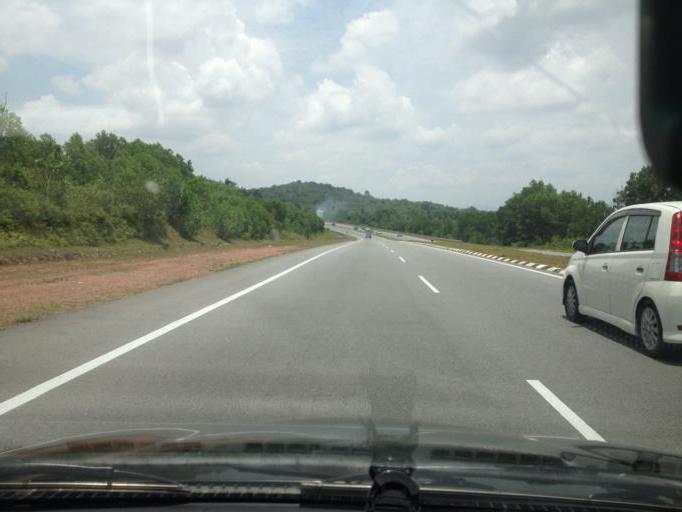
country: MY
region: Kedah
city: Sungai Petani
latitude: 5.6158
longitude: 100.5584
